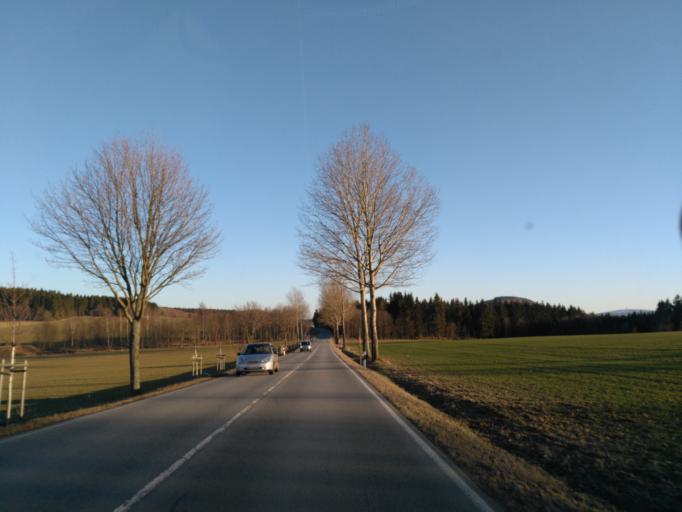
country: DE
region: Saxony
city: Konigswalde
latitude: 50.5400
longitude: 13.0226
